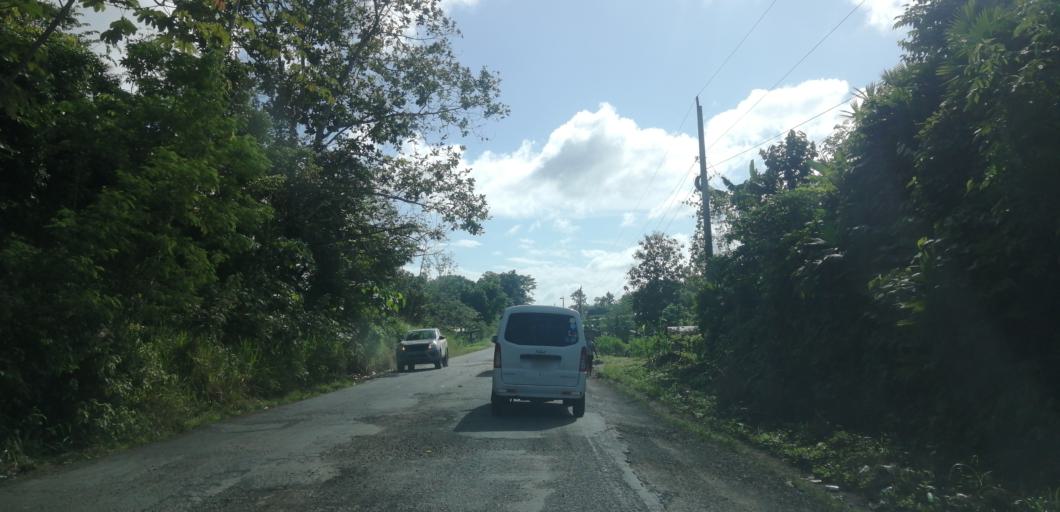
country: PA
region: Panama
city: Union Santena
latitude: 9.0493
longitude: -78.6370
